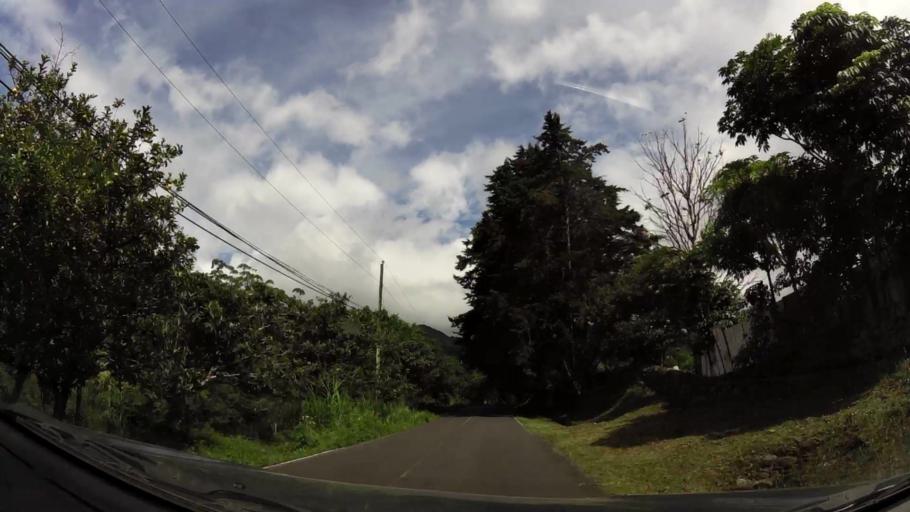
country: PA
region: Chiriqui
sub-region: Distrito Boquete
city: Boquete
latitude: 8.7947
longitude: -82.4287
